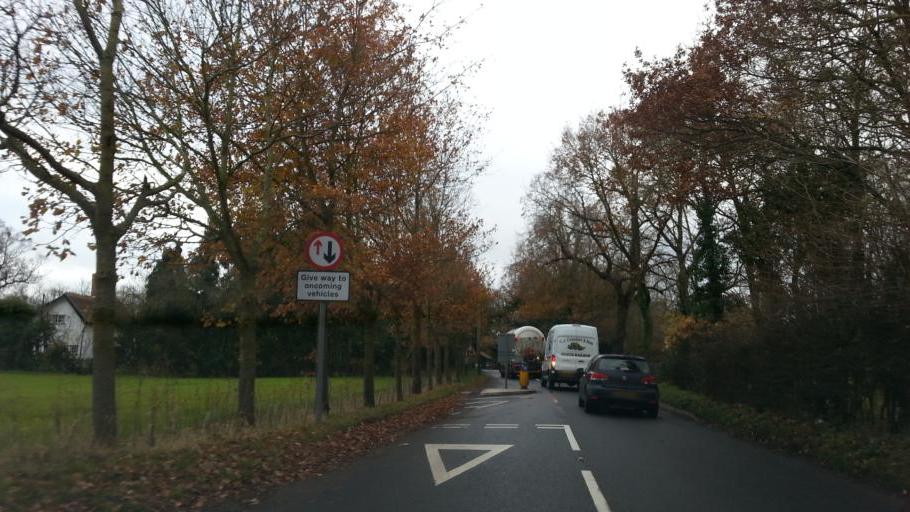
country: GB
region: England
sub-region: Norfolk
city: Diss
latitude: 52.3508
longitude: 1.2072
